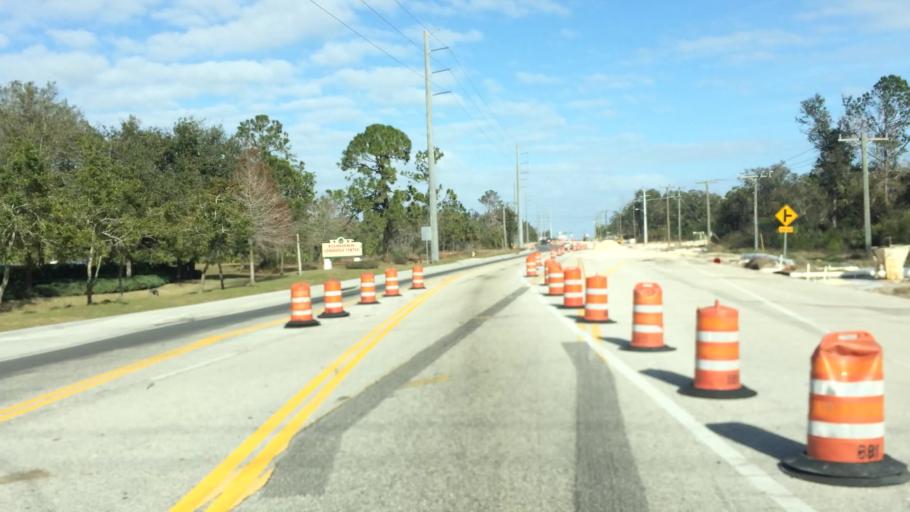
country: US
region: Florida
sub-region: Volusia County
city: Holly Hill
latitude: 29.2330
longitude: -81.0719
